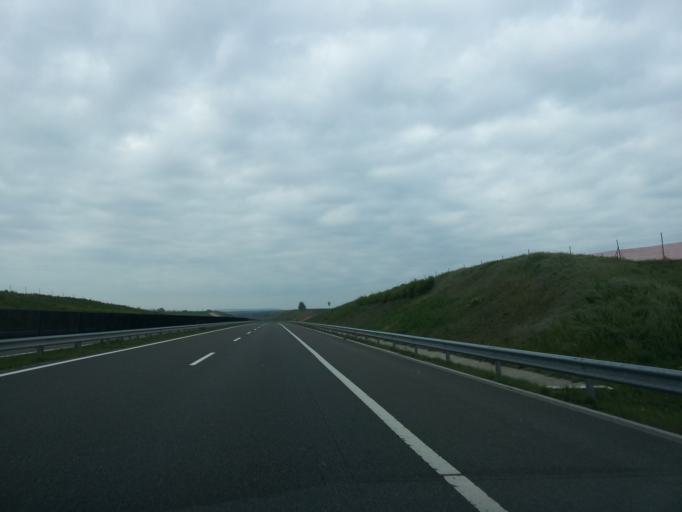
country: HU
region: Tolna
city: Paks
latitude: 46.6884
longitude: 18.8374
